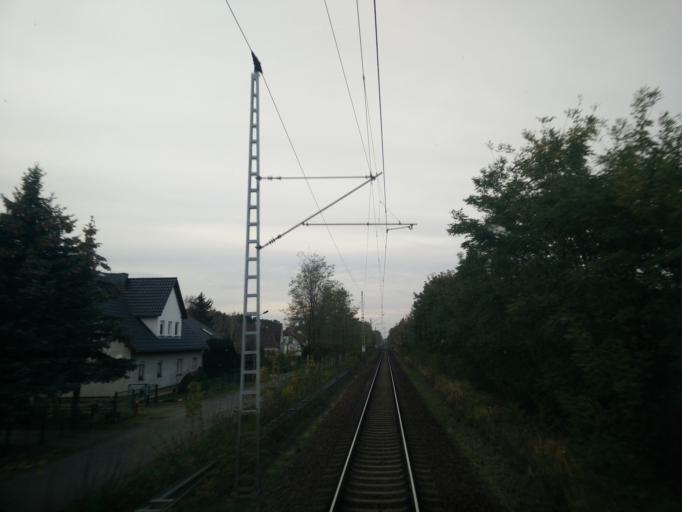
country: DE
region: Brandenburg
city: Vetschau
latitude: 51.8167
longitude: 14.0314
